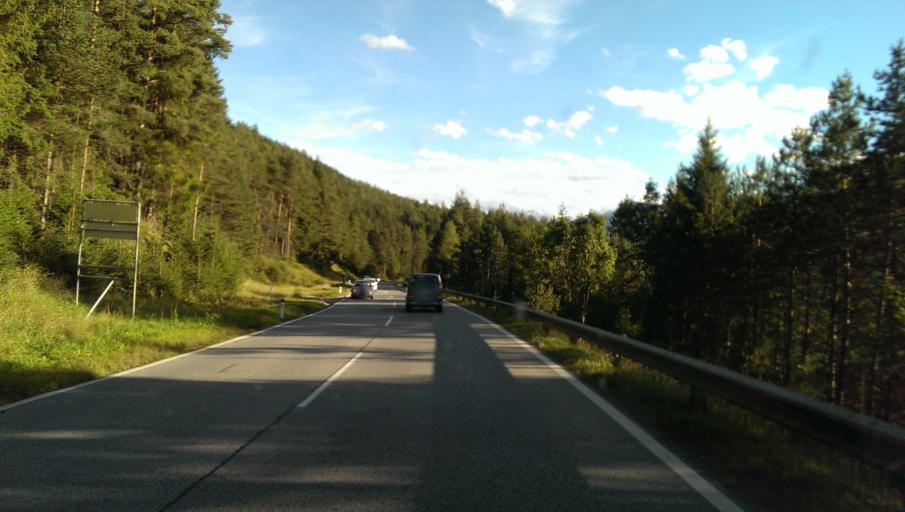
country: AT
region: Tyrol
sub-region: Politischer Bezirk Innsbruck Land
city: Reith bei Seefeld
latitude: 47.3119
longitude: 11.2014
